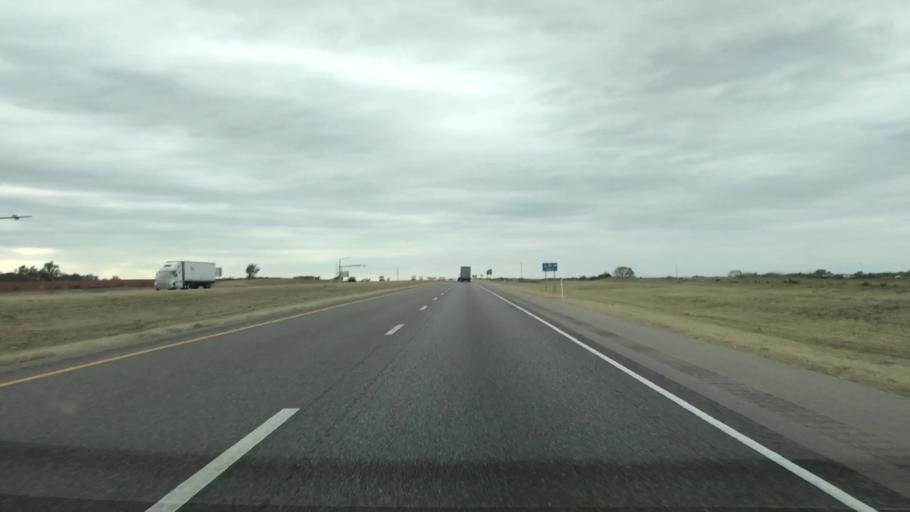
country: US
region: Oklahoma
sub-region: Beckham County
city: Erick
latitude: 35.2294
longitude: -99.9805
